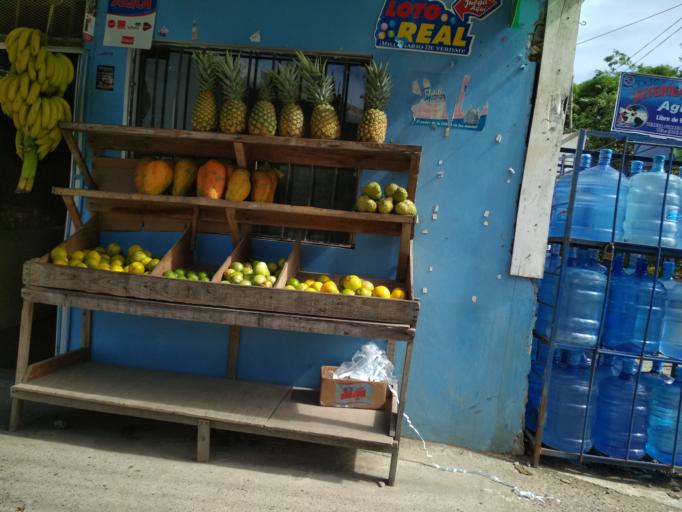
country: DO
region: Puerto Plata
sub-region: Puerto Plata
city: Puerto Plata
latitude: 19.8048
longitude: -70.7156
